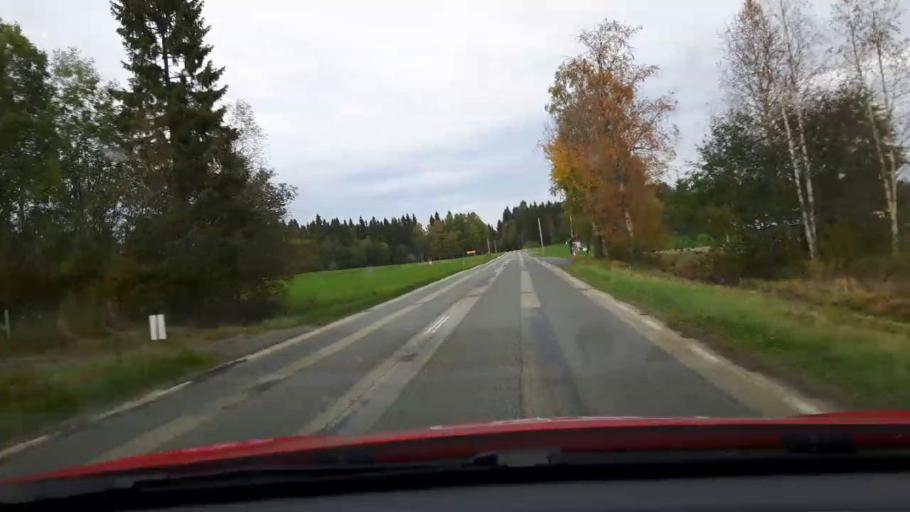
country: SE
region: Jaemtland
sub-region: Bergs Kommun
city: Hoverberg
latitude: 62.7807
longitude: 14.4325
